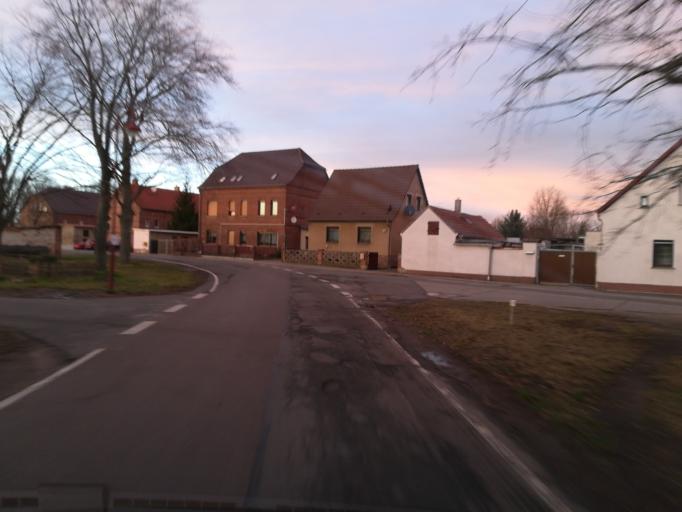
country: DE
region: Saxony-Anhalt
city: Brehna
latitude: 51.5260
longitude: 12.2289
